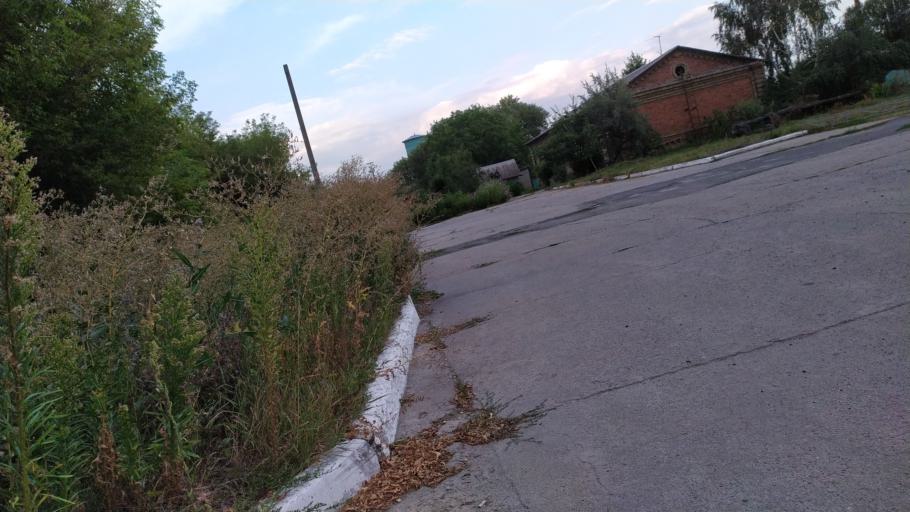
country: RU
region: Kursk
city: Kursk
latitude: 51.6560
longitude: 36.1369
